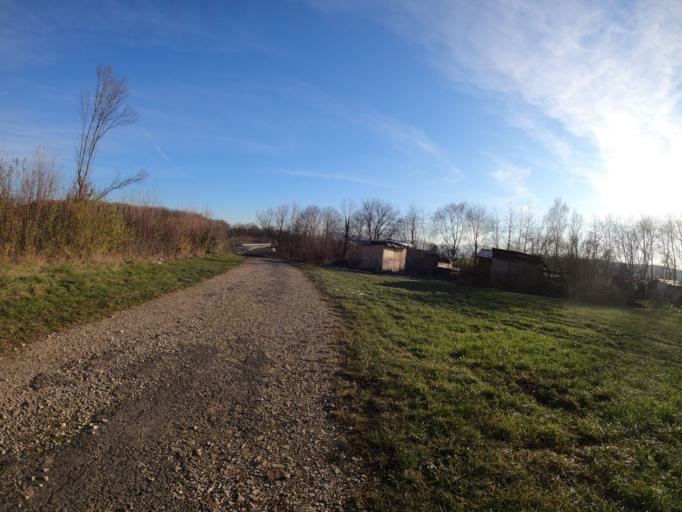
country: DE
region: Baden-Wuerttemberg
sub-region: Regierungsbezirk Stuttgart
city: Wangen
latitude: 48.6996
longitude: 9.6209
